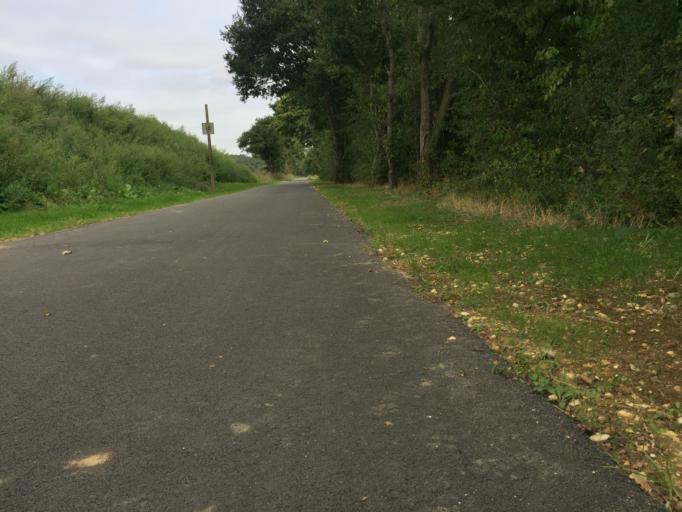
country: FR
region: Picardie
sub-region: Departement de l'Oise
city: Auneuil
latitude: 49.3911
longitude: 2.0074
